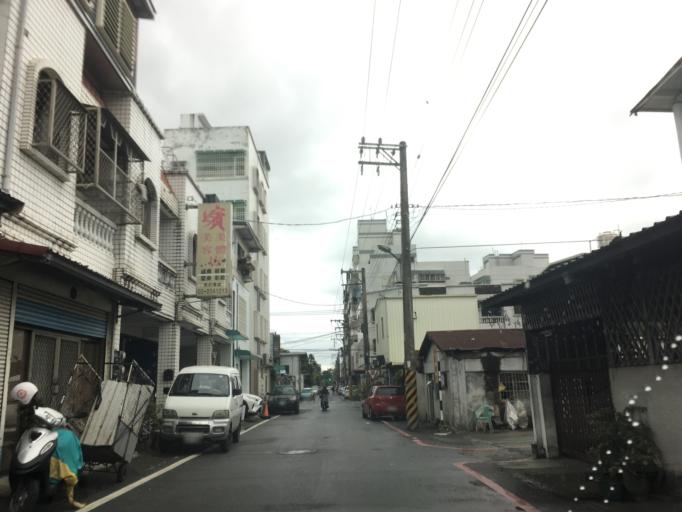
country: TW
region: Taiwan
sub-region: Hualien
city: Hualian
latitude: 23.9713
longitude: 121.5799
